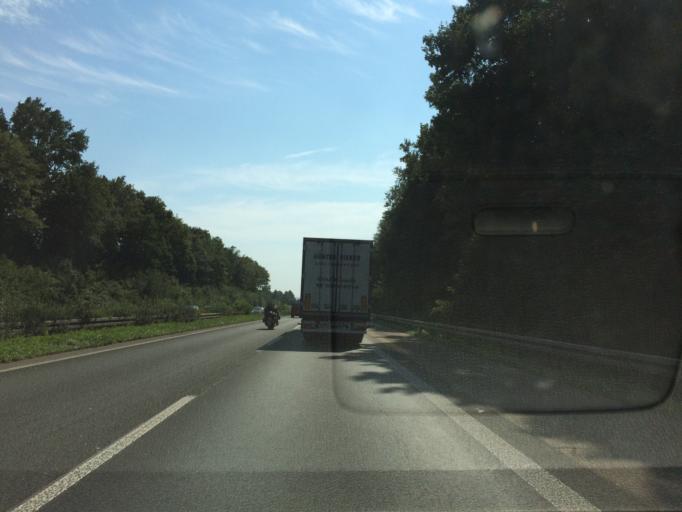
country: DE
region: North Rhine-Westphalia
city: Kamen
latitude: 51.6128
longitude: 7.6899
